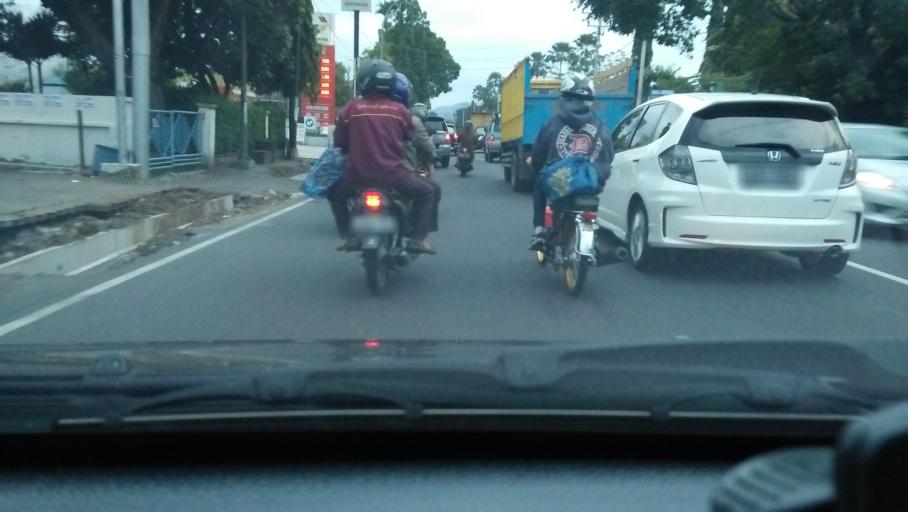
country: ID
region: Central Java
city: Magelang
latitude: -7.4603
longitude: 110.2226
